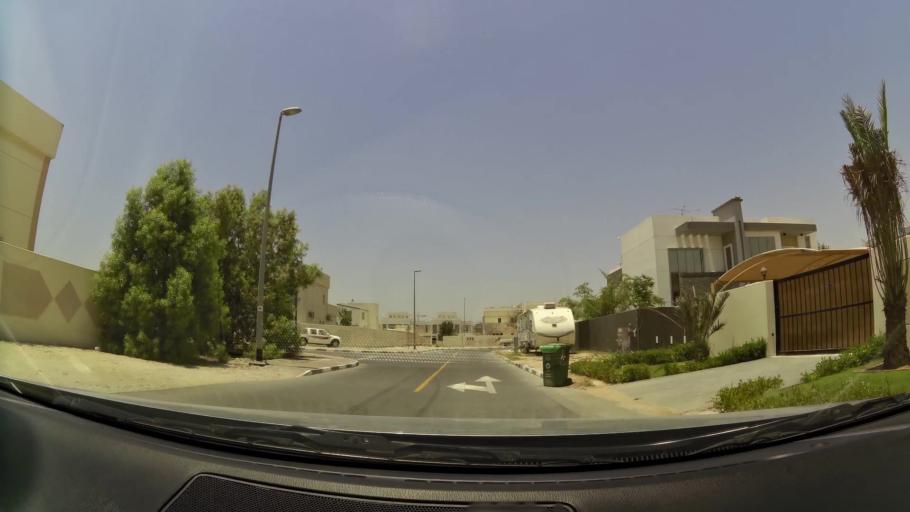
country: AE
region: Dubai
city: Dubai
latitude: 25.1038
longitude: 55.1954
